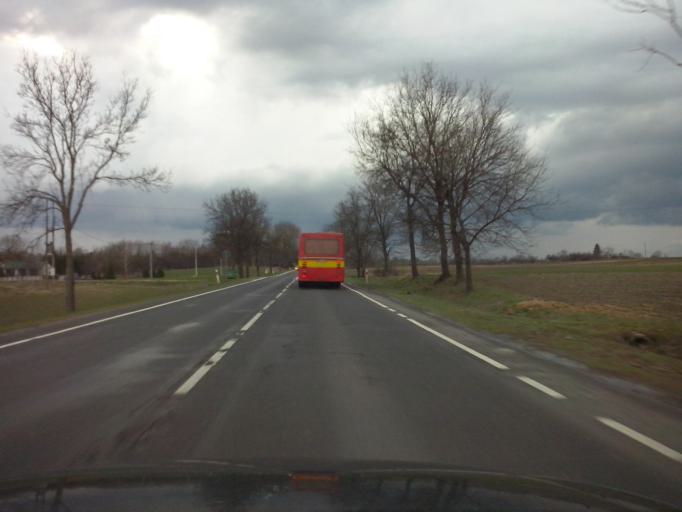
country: PL
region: Lublin Voivodeship
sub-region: Powiat chelmski
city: Rejowiec Fabryczny
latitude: 51.1723
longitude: 23.2914
